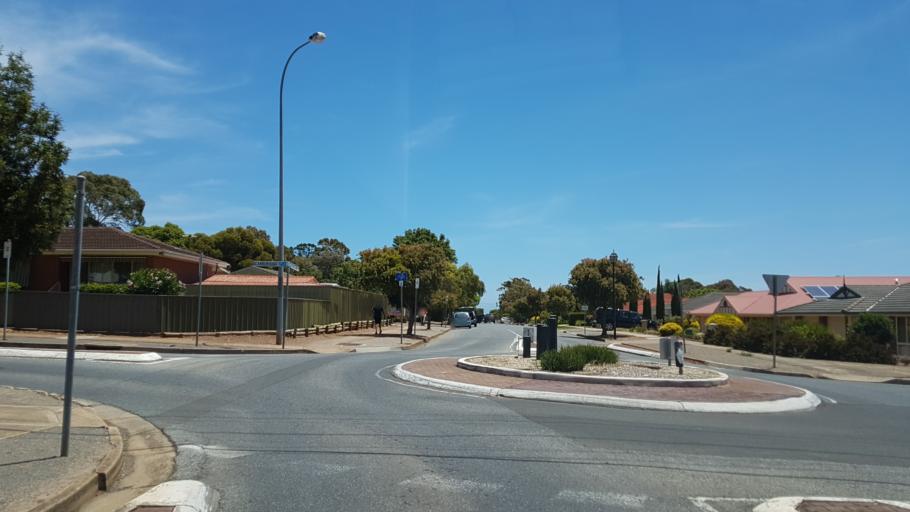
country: AU
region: South Australia
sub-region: Holdfast Bay
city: Seacliff Park
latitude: -35.0255
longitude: 138.5381
